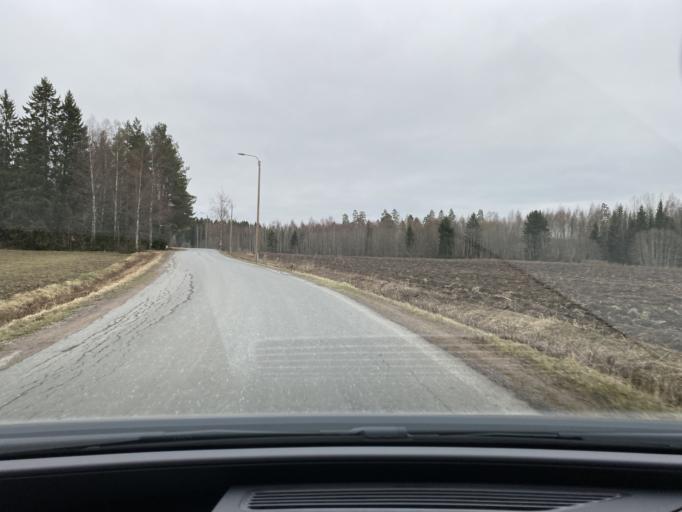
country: FI
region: Satakunta
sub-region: Pori
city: Huittinen
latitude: 61.1669
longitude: 22.7214
